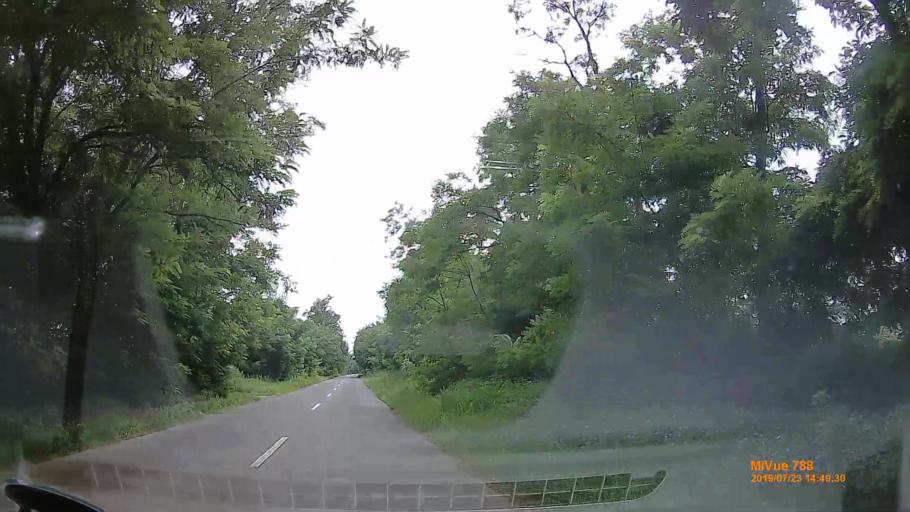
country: HU
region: Szabolcs-Szatmar-Bereg
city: Kalmanhaza
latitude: 47.8953
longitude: 21.6622
